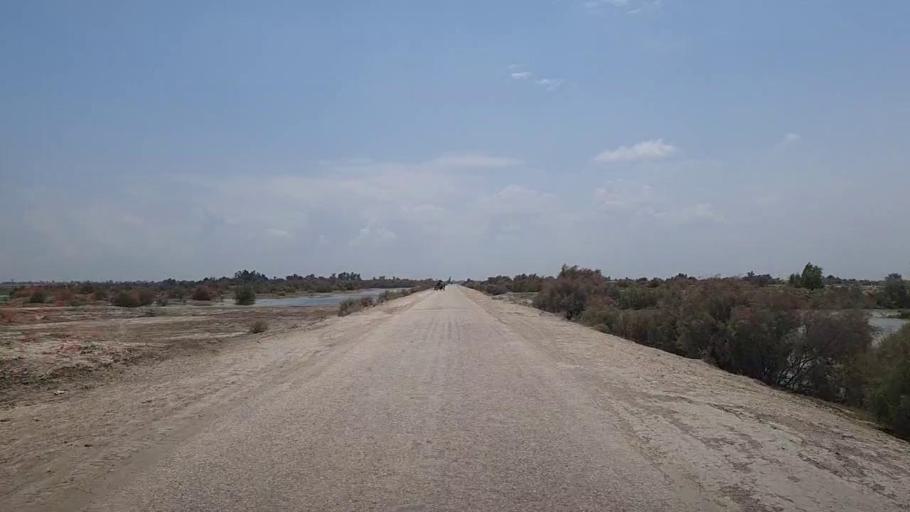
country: PK
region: Sindh
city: Kandhkot
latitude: 28.2859
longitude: 69.1662
